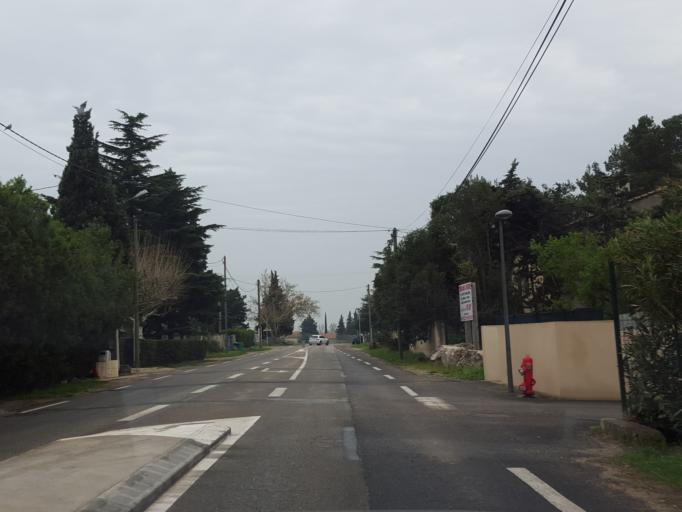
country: FR
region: Provence-Alpes-Cote d'Azur
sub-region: Departement du Vaucluse
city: Morieres-les-Avignon
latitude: 43.9278
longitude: 4.9015
